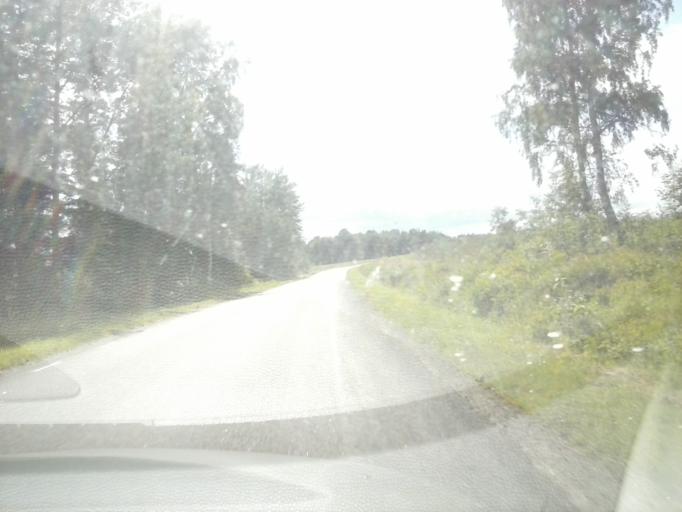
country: EE
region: Laeaene-Virumaa
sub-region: Tamsalu vald
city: Tamsalu
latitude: 59.0751
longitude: 26.1335
